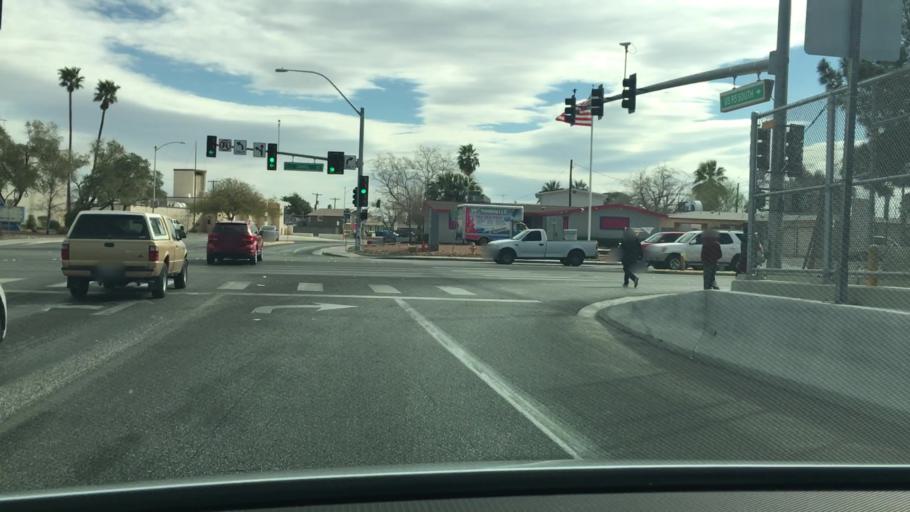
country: US
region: Nevada
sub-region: Clark County
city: Spring Valley
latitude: 36.1728
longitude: -115.2246
